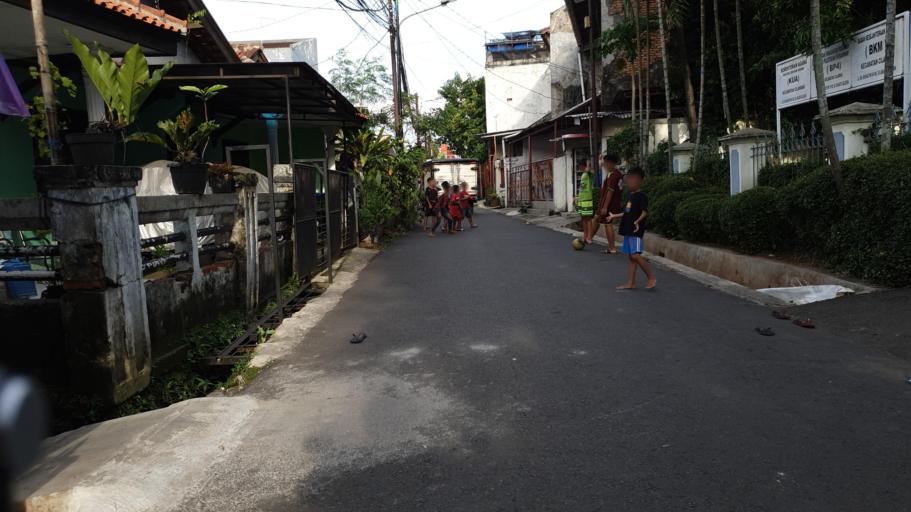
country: ID
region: Banten
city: South Tangerang
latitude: -6.2902
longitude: 106.7888
